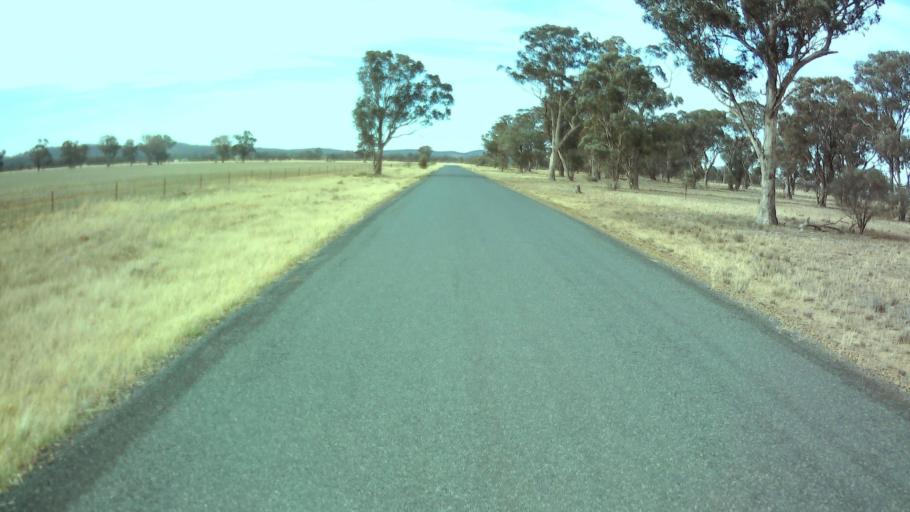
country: AU
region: New South Wales
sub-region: Weddin
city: Grenfell
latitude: -33.8598
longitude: 147.8601
